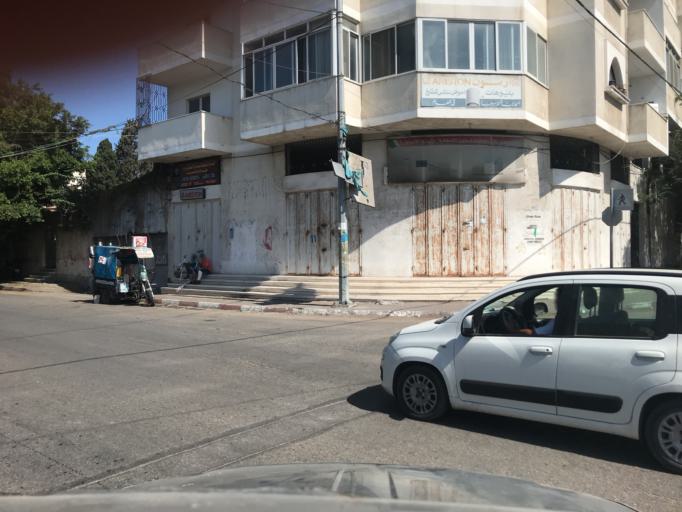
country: PS
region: Gaza Strip
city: Gaza
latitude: 31.5211
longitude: 34.4495
